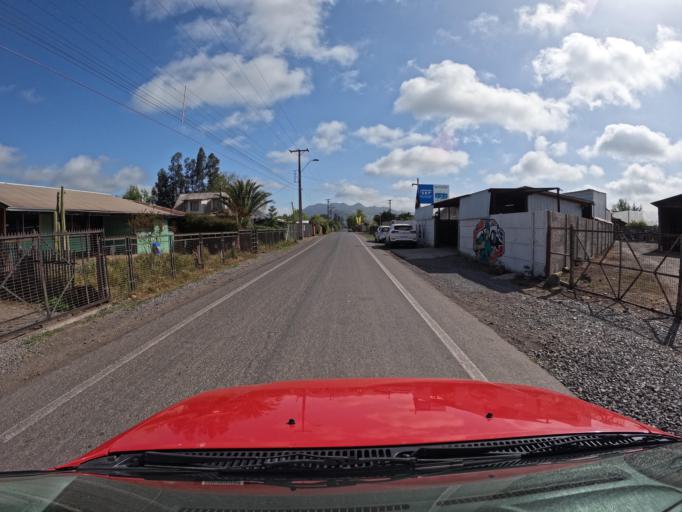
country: CL
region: Maule
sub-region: Provincia de Curico
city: Teno
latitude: -34.8792
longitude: -71.2259
